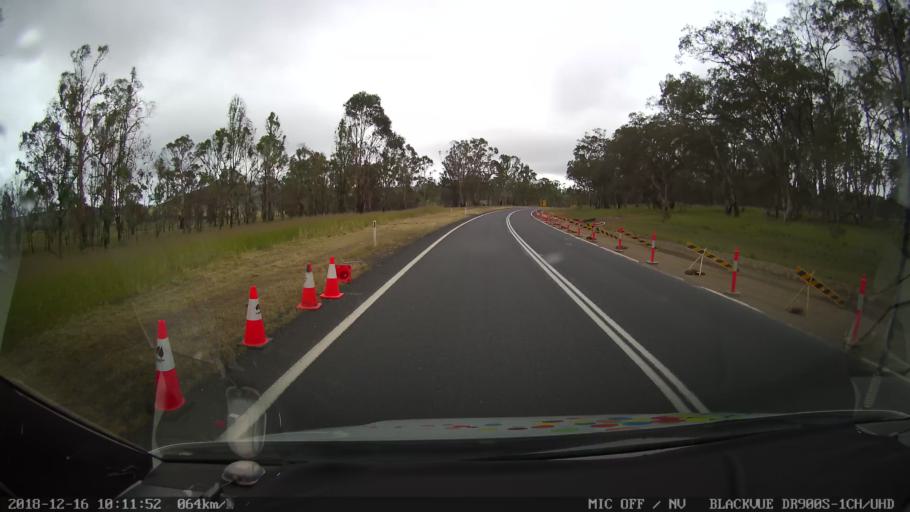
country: AU
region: New South Wales
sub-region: Glen Innes Severn
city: Glen Innes
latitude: -29.3101
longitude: 151.9352
